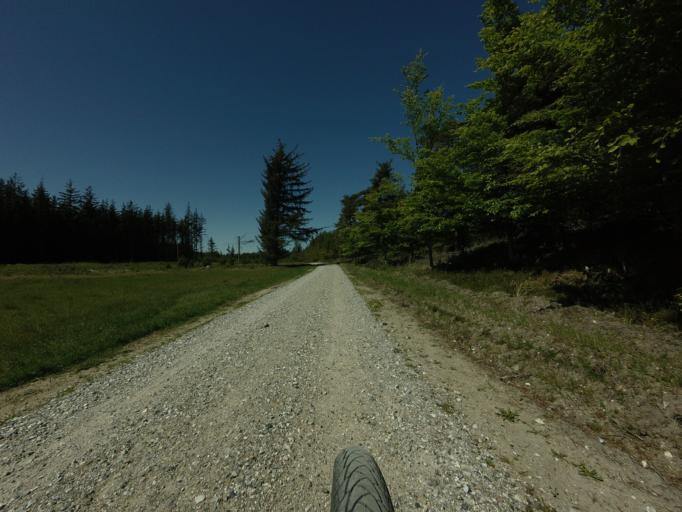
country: DK
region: North Denmark
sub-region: Jammerbugt Kommune
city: Pandrup
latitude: 57.2422
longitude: 9.5924
